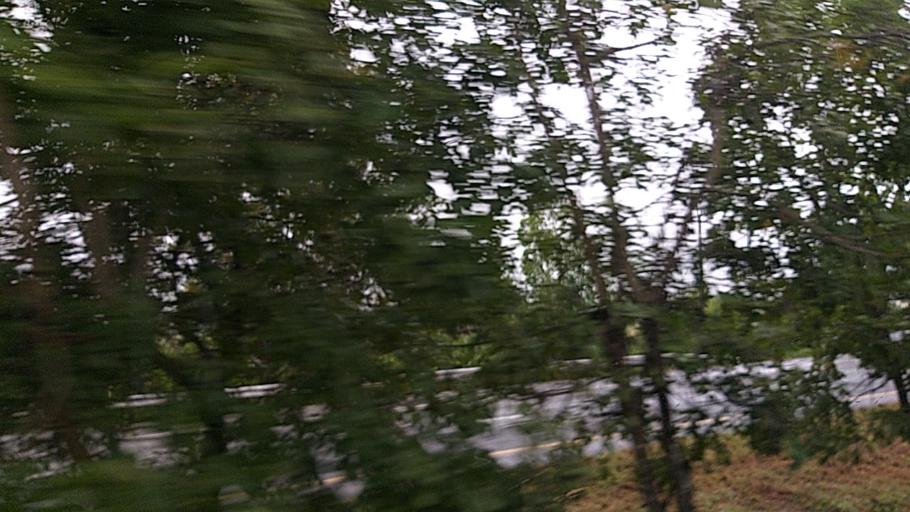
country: TH
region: Nakhon Ratchasima
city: Non Sung
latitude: 15.1381
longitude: 102.3120
